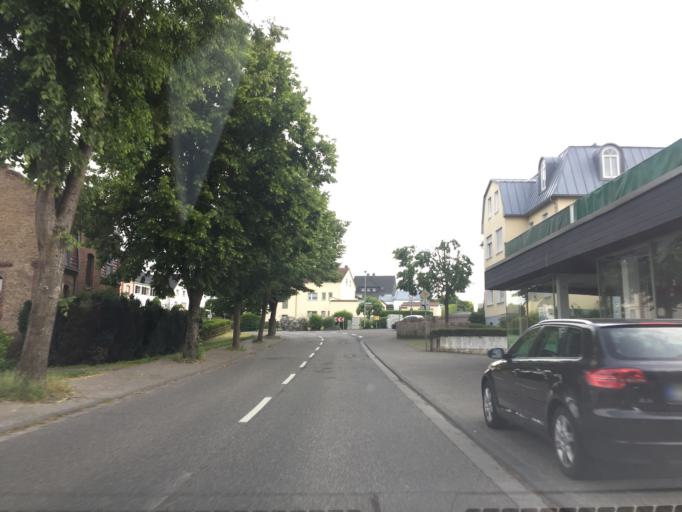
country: DE
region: Hesse
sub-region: Regierungsbezirk Giessen
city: Elz
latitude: 50.4450
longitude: 8.0413
